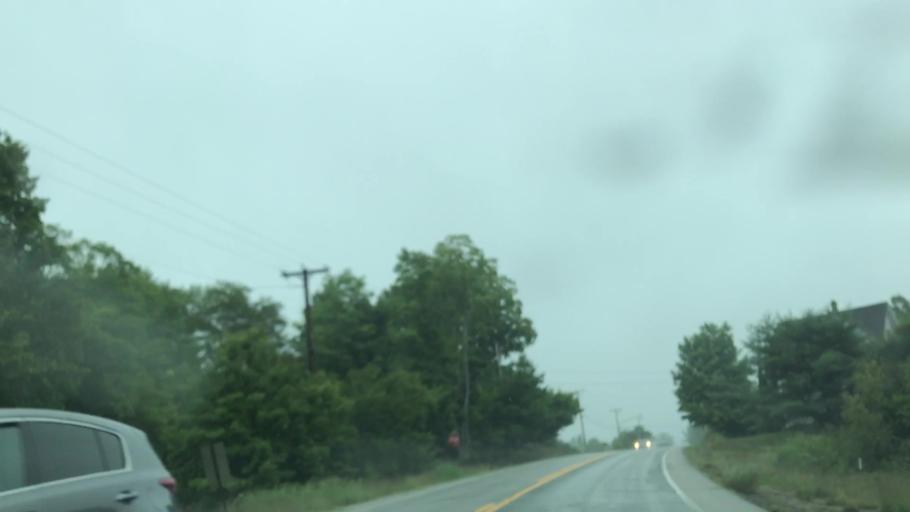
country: US
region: Maine
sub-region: York County
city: North Berwick
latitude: 43.2998
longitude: -70.7653
